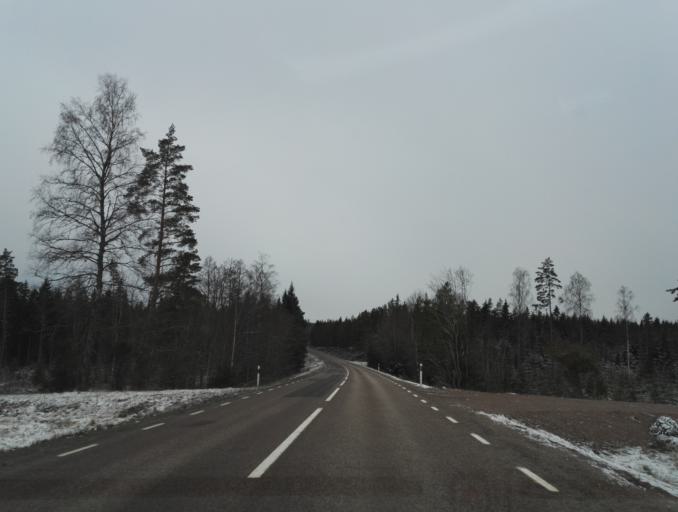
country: SE
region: Kalmar
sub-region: Hultsfreds Kommun
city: Virserum
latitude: 57.2570
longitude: 15.5473
